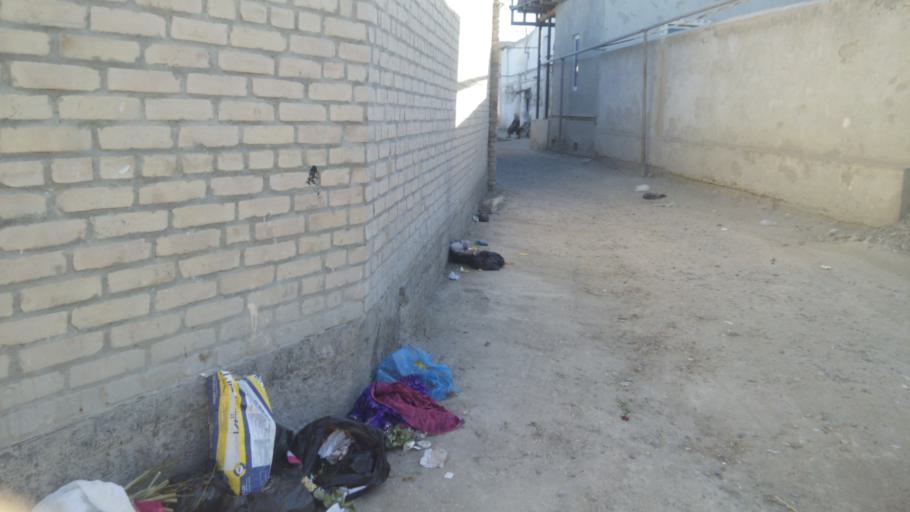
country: UZ
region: Bukhara
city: Bukhara
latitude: 39.7751
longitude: 64.4254
